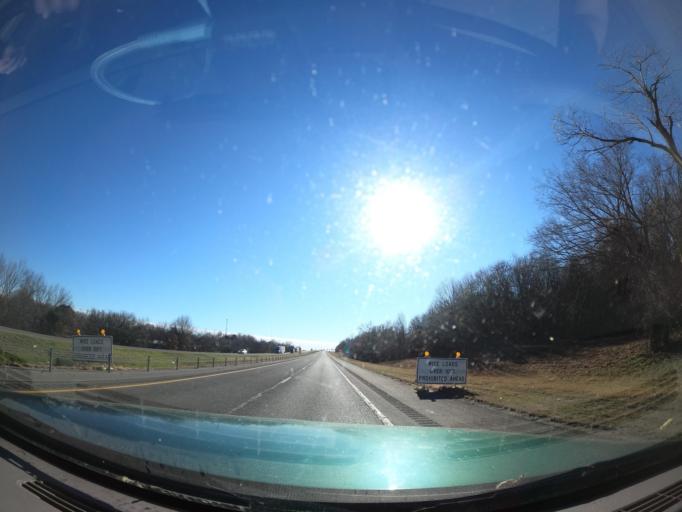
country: US
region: Oklahoma
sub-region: McIntosh County
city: Eufaula
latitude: 35.3700
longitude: -95.5721
